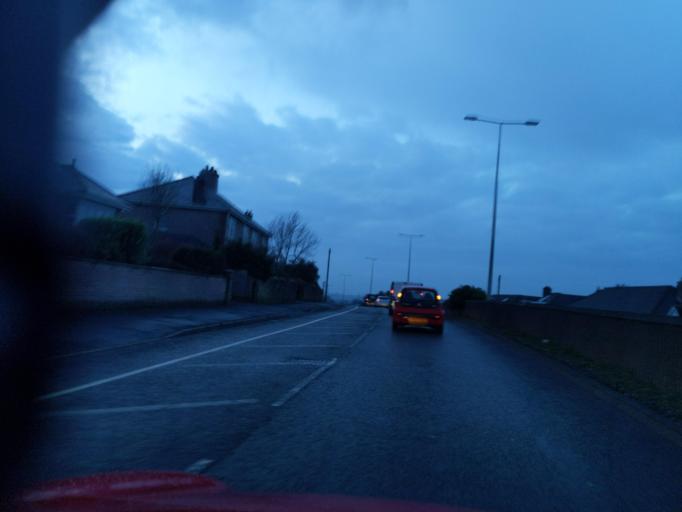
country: GB
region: England
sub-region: Plymouth
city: Plymstock
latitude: 50.3621
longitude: -4.0674
